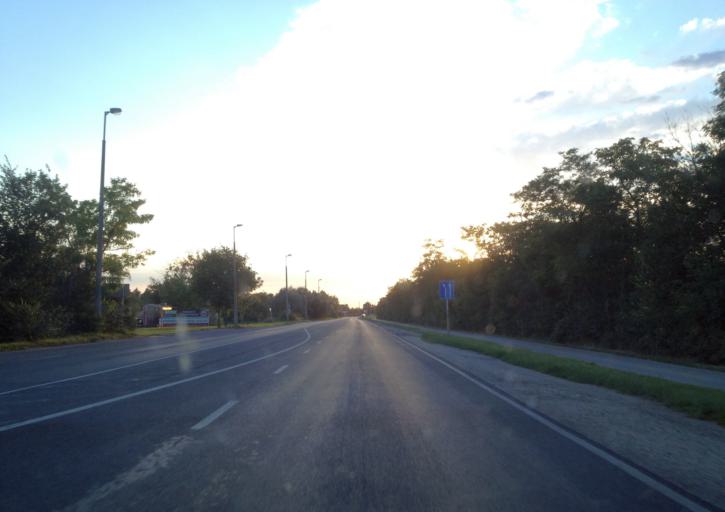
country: HU
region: Gyor-Moson-Sopron
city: Mosonmagyarovar
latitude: 47.8961
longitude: 17.2143
